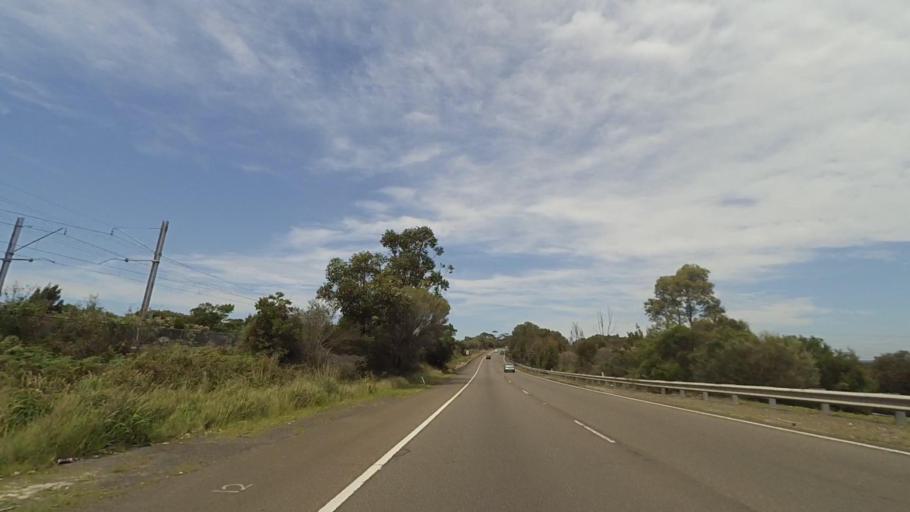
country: AU
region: New South Wales
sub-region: Sutherland Shire
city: Heathcote
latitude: -34.1083
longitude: 150.9937
